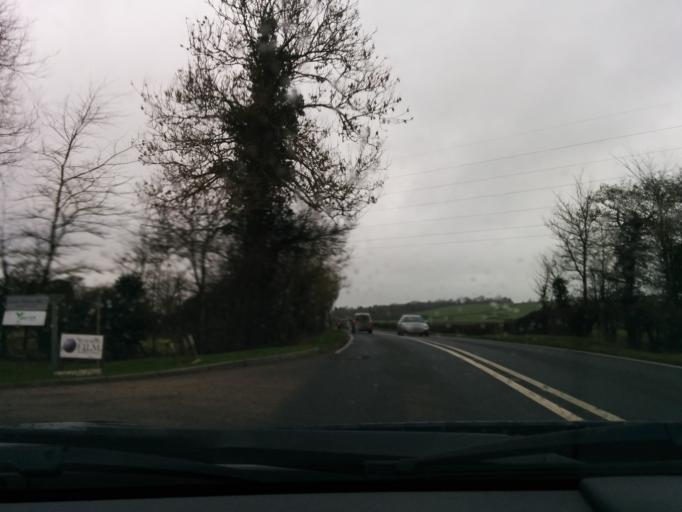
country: GB
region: England
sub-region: Oxfordshire
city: Eynsham
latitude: 51.7584
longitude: -1.3406
